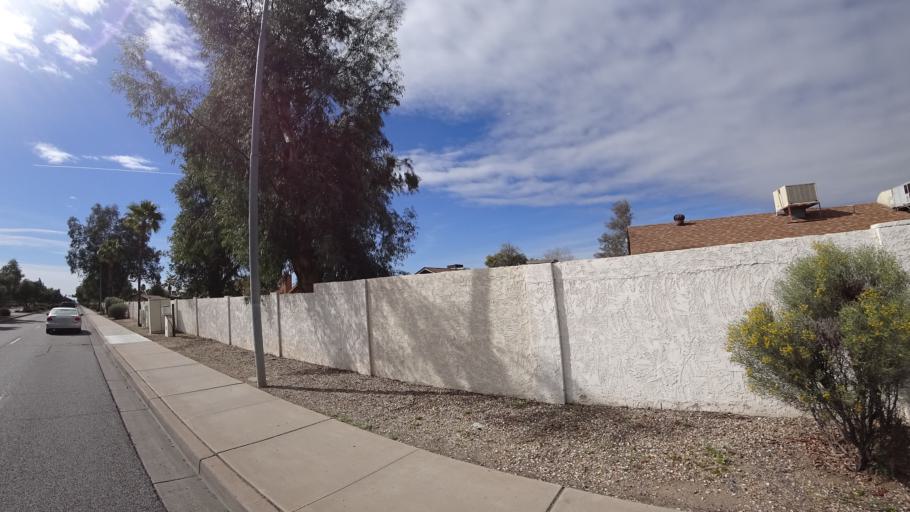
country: US
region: Arizona
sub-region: Maricopa County
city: Peoria
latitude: 33.6202
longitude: -112.1859
